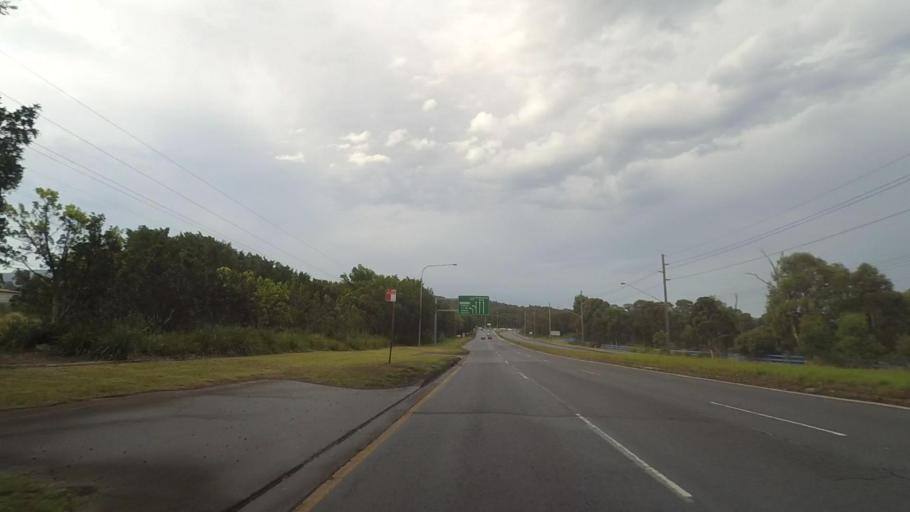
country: AU
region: New South Wales
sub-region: Wollongong
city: Mount Saint Thomas
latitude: -34.4497
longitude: 150.8747
